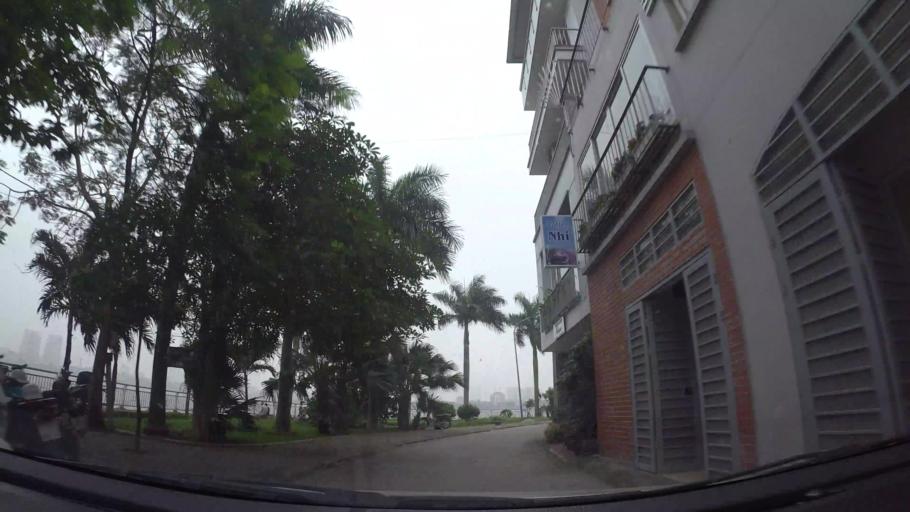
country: VN
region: Ha Noi
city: Tay Ho
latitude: 21.0543
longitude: 105.8206
